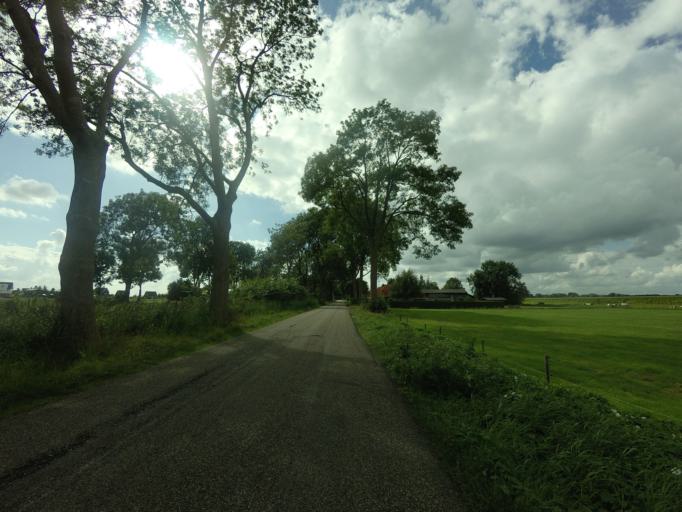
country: NL
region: Overijssel
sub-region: Gemeente Steenwijkerland
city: Giethoorn
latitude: 52.7221
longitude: 6.0687
